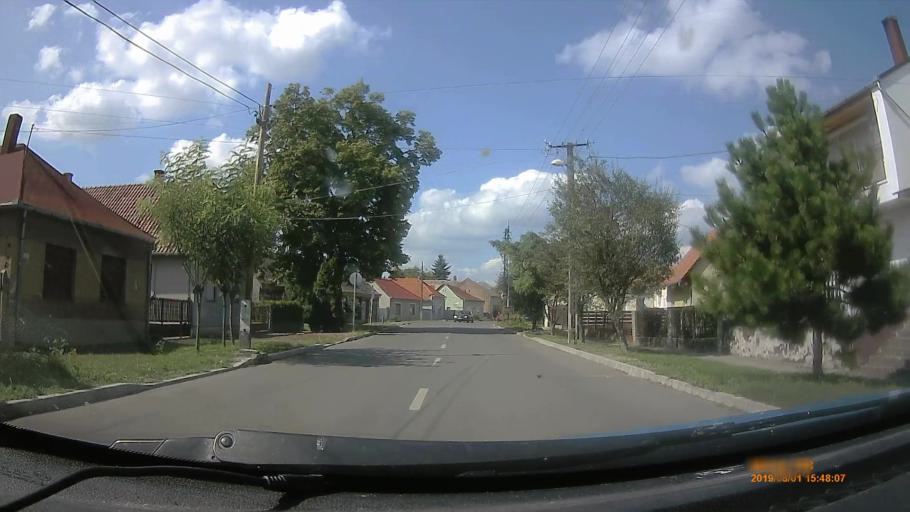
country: HU
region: Baranya
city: Szentlorinc
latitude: 46.0357
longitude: 17.9849
